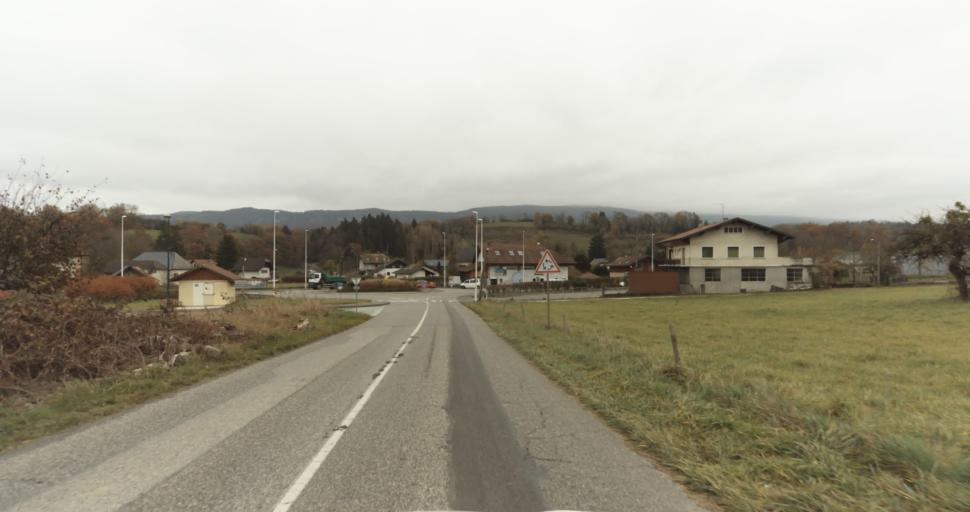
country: FR
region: Rhone-Alpes
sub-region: Departement de la Haute-Savoie
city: Seynod
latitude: 45.8639
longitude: 6.0679
